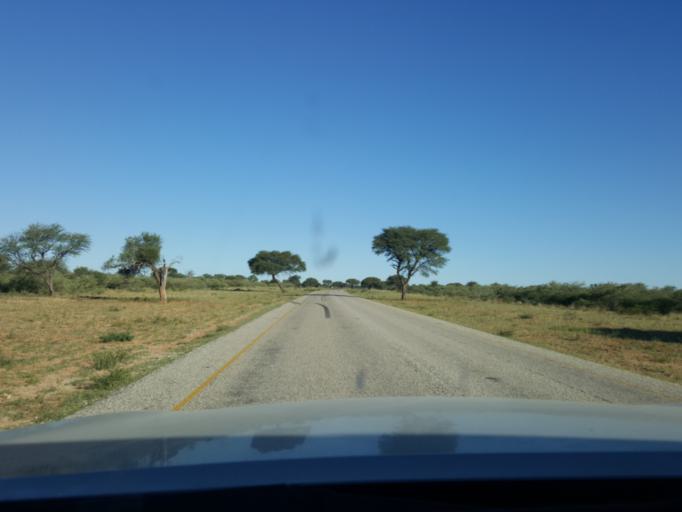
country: BW
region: Kgalagadi
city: Kang
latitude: -24.0231
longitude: 23.0377
